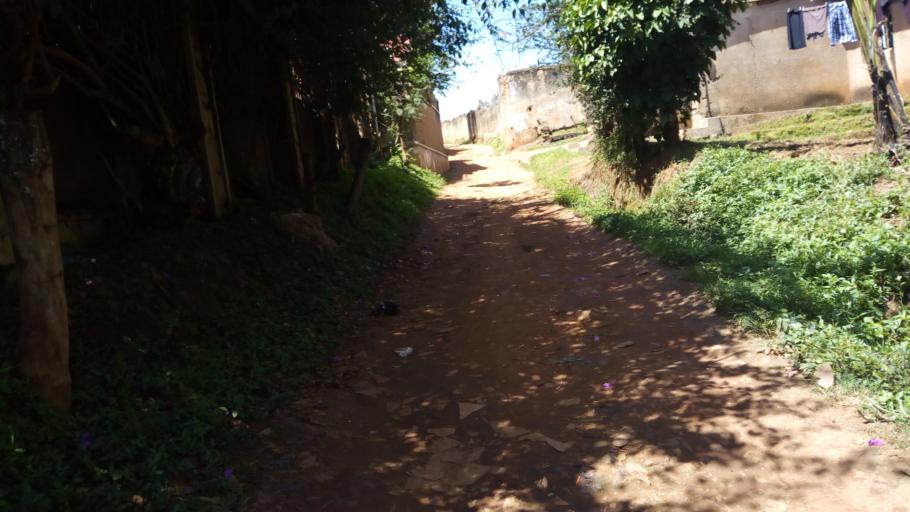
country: UG
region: Central Region
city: Kampala Central Division
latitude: 0.3591
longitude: 32.5574
